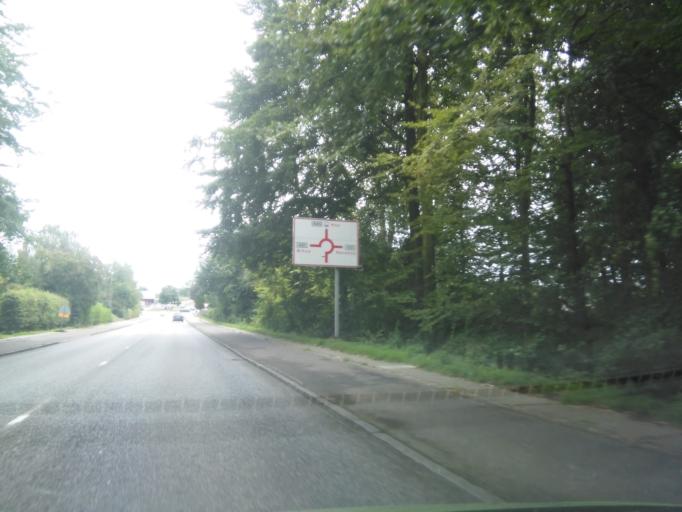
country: DK
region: Central Jutland
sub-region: Odder Kommune
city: Odder
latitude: 55.9678
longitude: 10.1451
